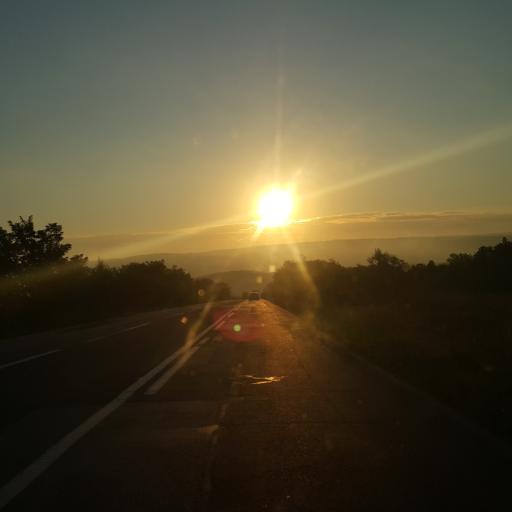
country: RS
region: Central Serbia
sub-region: Zajecarski Okrug
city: Zajecar
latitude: 44.0248
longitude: 22.3109
